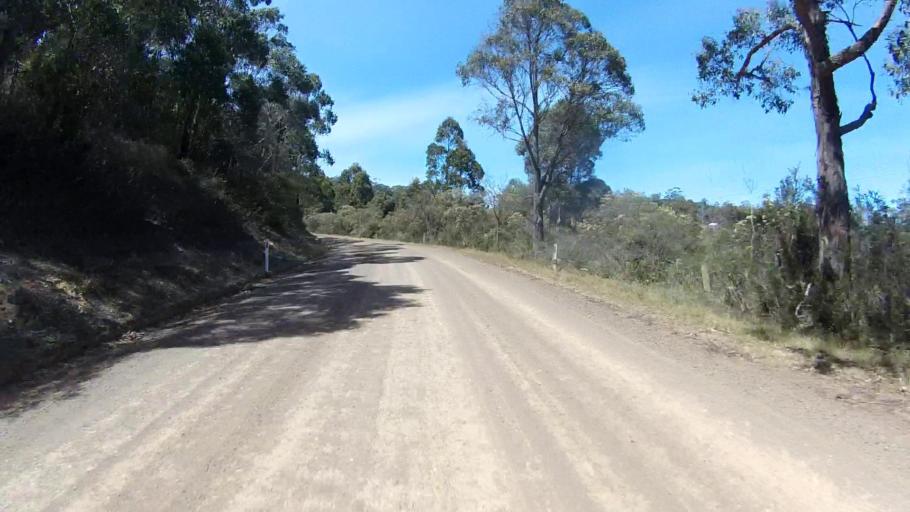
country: AU
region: Tasmania
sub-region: Sorell
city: Sorell
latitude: -42.6987
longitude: 147.7411
